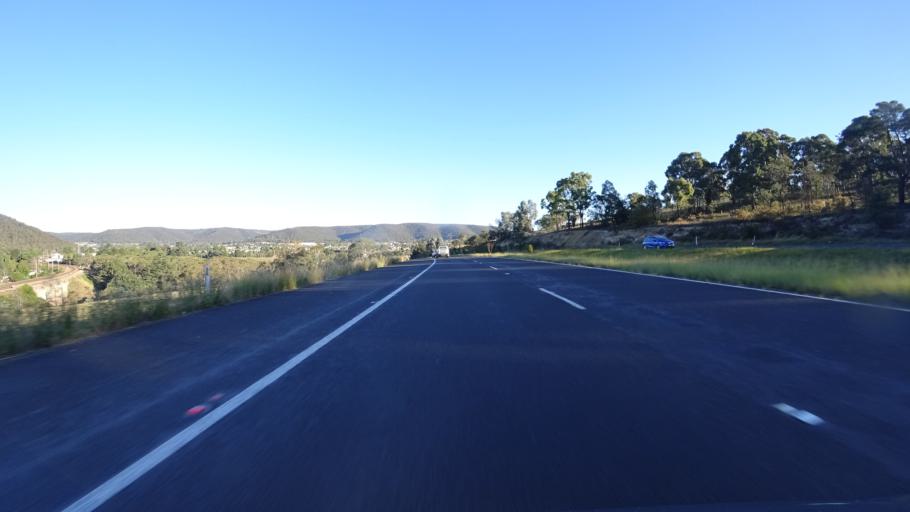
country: AU
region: New South Wales
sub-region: Lithgow
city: Lithgow
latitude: -33.4720
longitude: 150.1244
